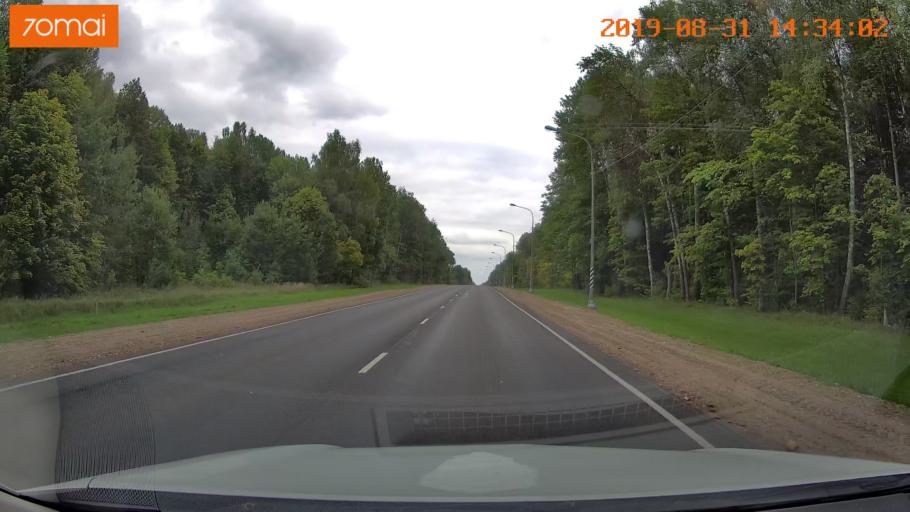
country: RU
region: Smolensk
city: Yekimovichi
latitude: 54.1552
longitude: 33.4302
